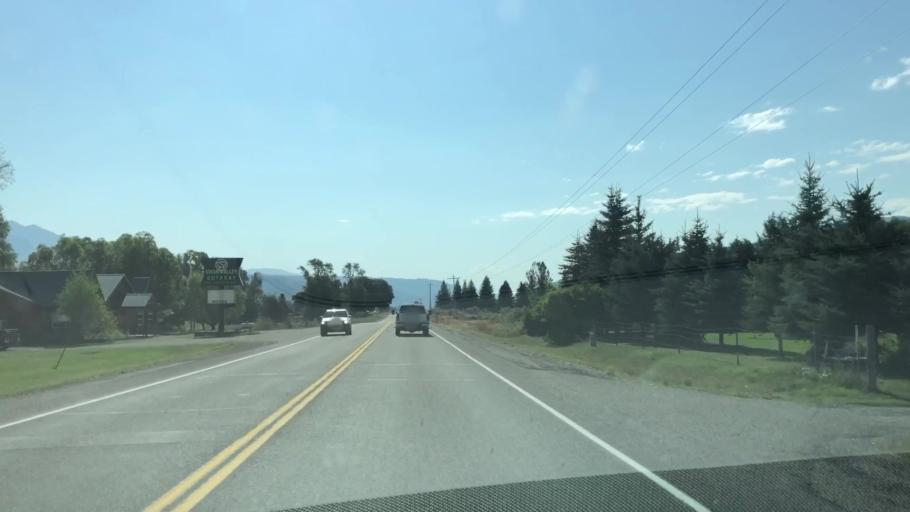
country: US
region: Idaho
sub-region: Teton County
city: Victor
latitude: 43.4024
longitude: -111.2897
